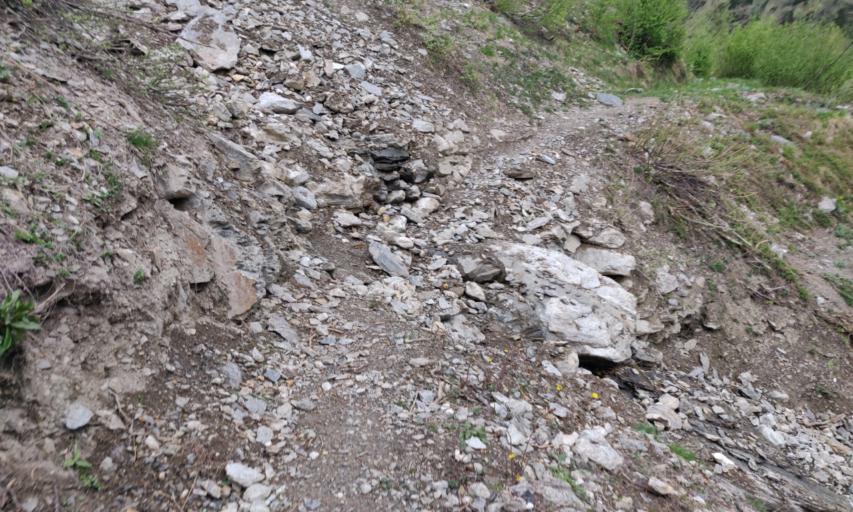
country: CH
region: Valais
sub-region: Visp District
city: Baltschieder
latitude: 46.3336
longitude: 7.8780
